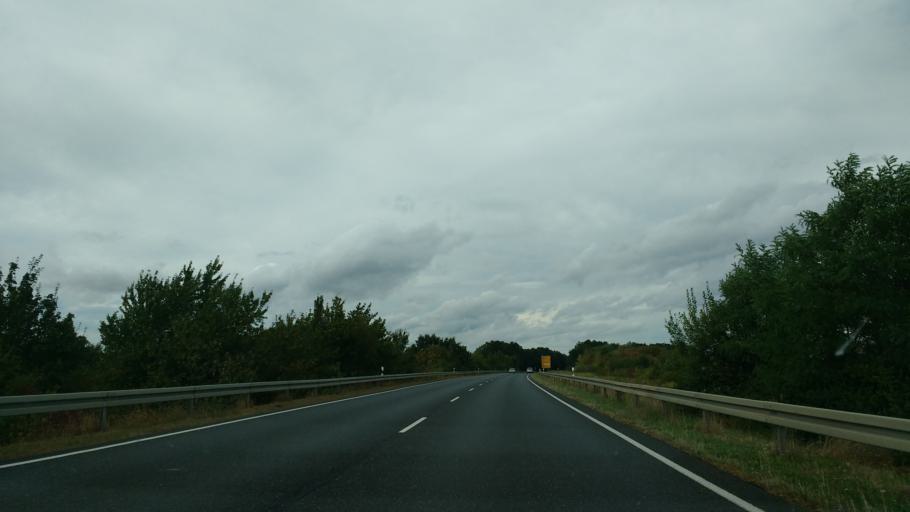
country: DE
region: Bavaria
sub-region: Regierungsbezirk Unterfranken
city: Schwebheim
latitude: 49.9850
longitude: 10.2432
